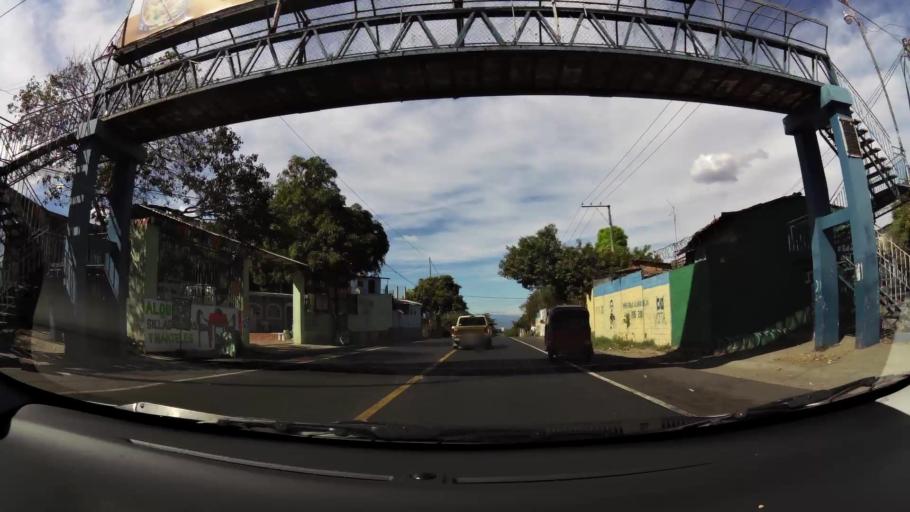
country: SV
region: San Salvador
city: Guazapa
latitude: 13.8744
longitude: -89.1729
